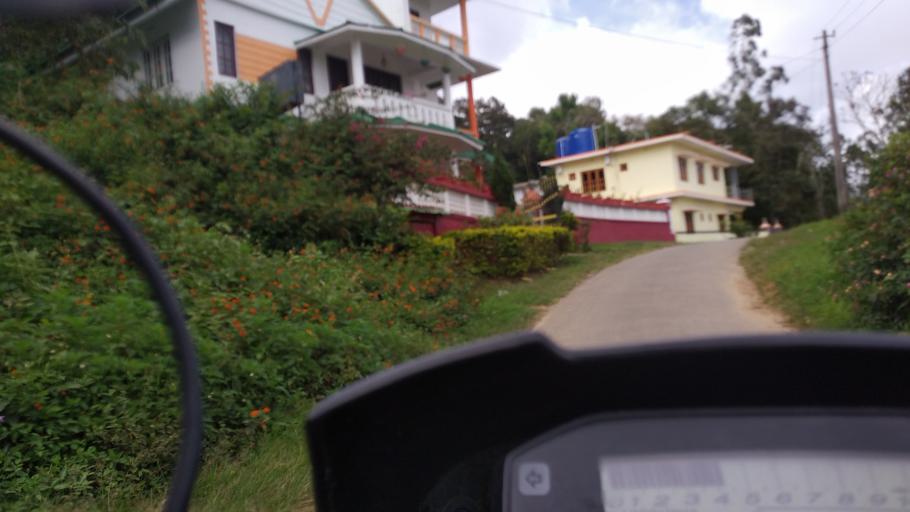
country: IN
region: Kerala
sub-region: Idukki
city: Munnar
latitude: 10.0396
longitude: 77.1742
